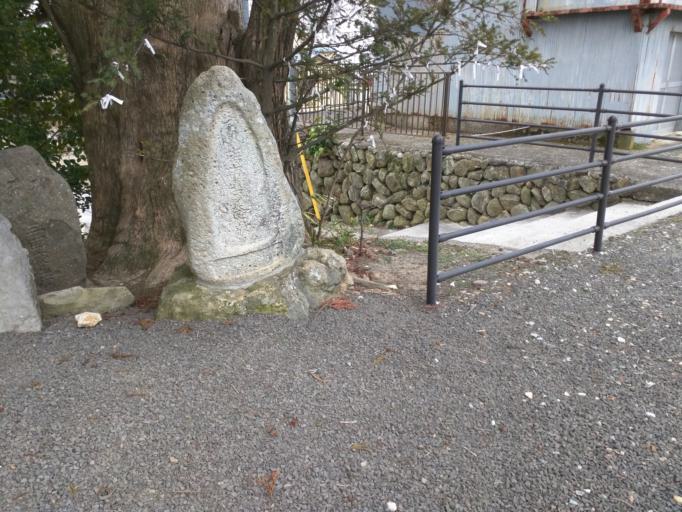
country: JP
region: Fukushima
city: Fukushima-shi
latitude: 37.8333
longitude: 140.4505
